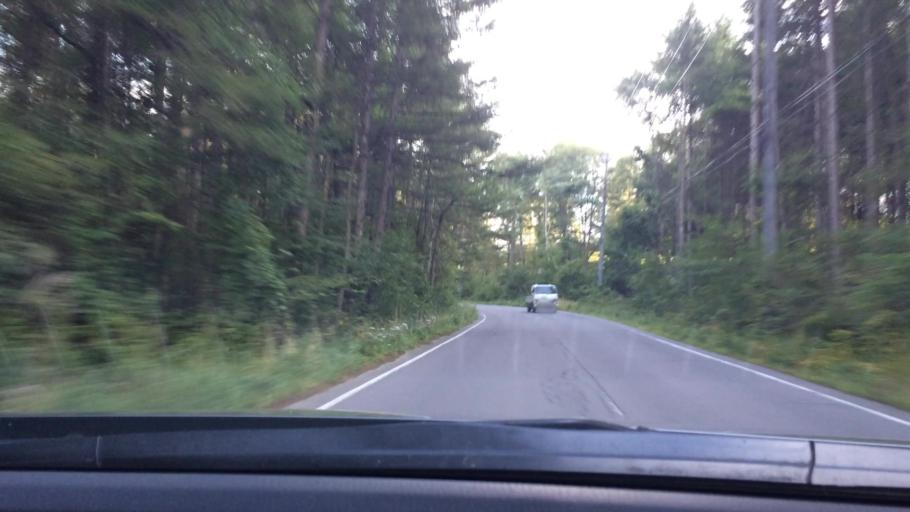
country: JP
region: Nagano
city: Komoro
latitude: 36.4855
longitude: 138.5174
